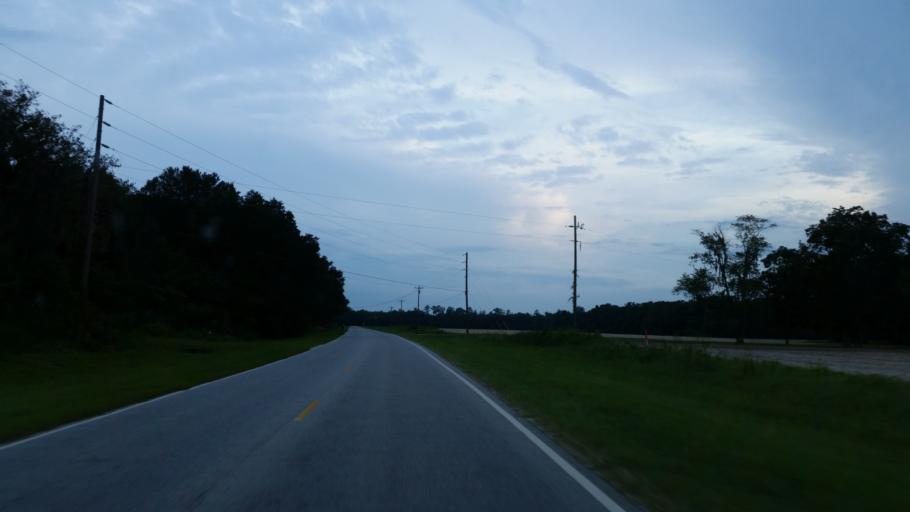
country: US
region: Georgia
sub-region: Echols County
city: Statenville
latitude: 30.6576
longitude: -83.1843
